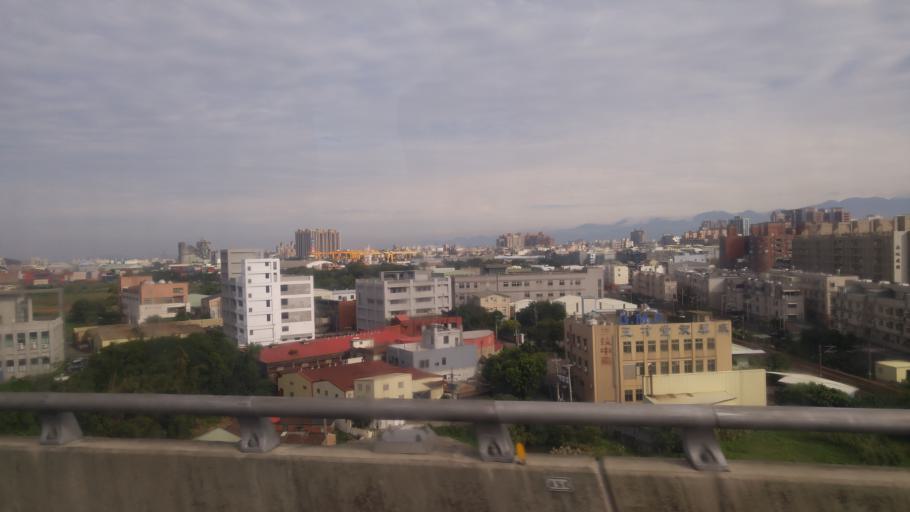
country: TW
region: Taiwan
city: Daxi
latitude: 24.9141
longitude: 121.1666
